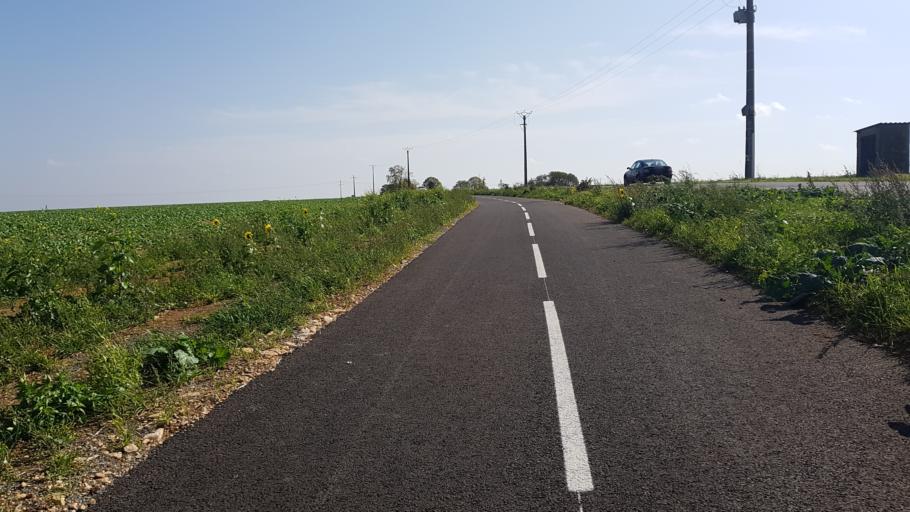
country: FR
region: Poitou-Charentes
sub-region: Departement de la Vienne
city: Chasseneuil-du-Poitou
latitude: 46.6589
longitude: 0.3453
